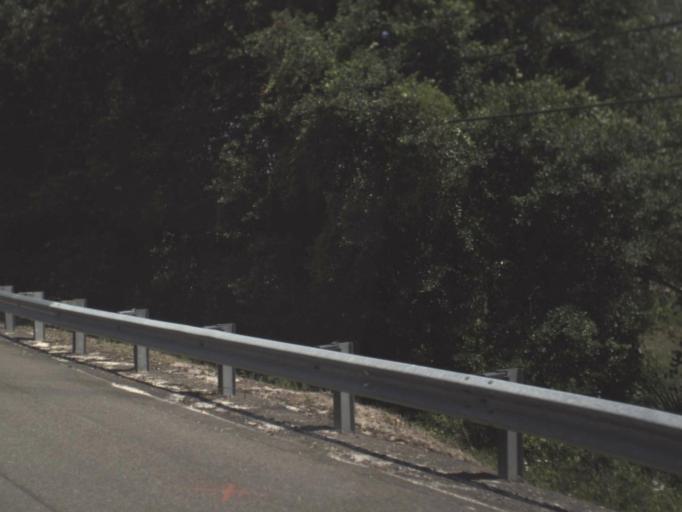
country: US
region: Florida
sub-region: Clay County
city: Keystone Heights
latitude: 29.8035
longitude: -82.0603
